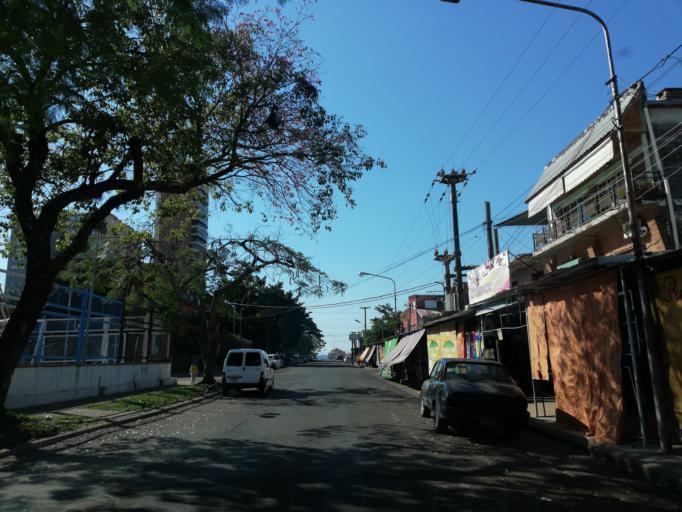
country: AR
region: Misiones
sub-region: Departamento de Capital
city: Posadas
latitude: -27.3655
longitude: -55.8867
